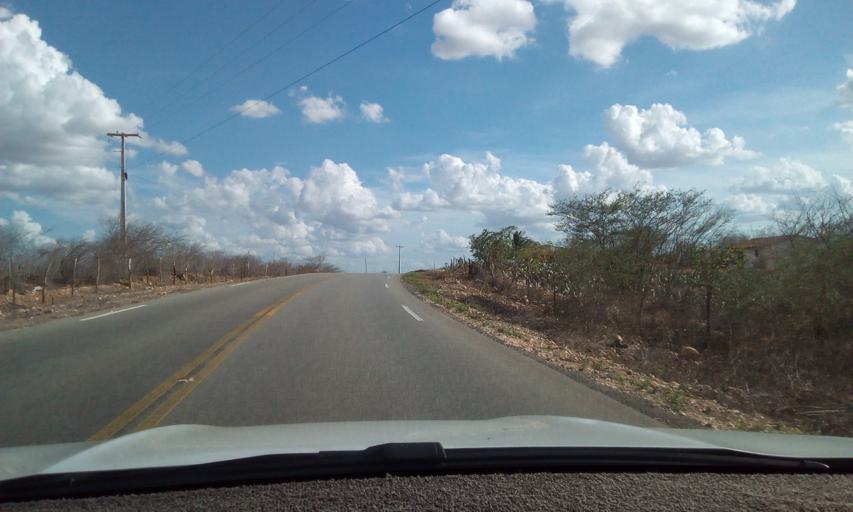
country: BR
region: Paraiba
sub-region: Soledade
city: Soledade
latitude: -6.8026
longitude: -36.4031
